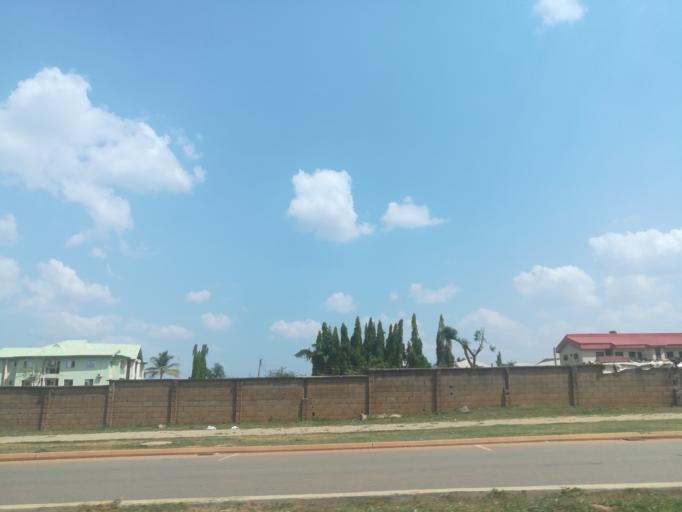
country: NG
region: Abuja Federal Capital Territory
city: Abuja
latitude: 9.0498
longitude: 7.4440
